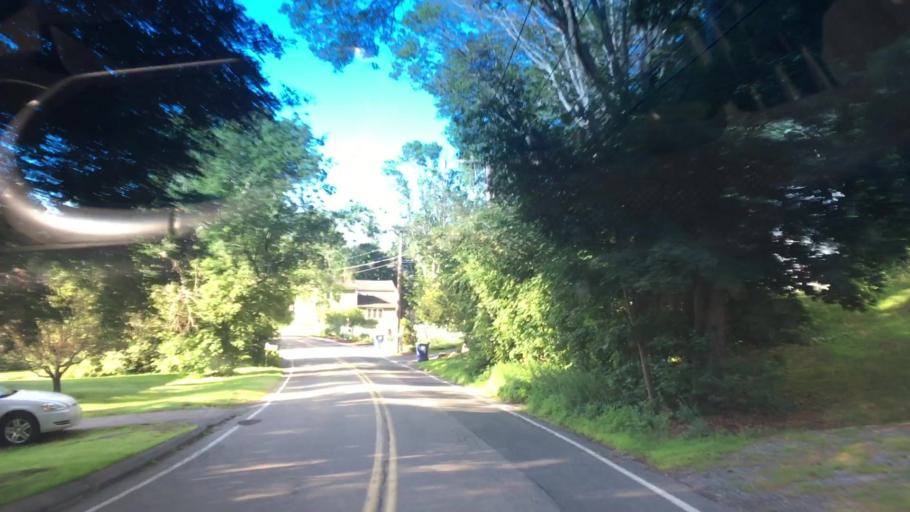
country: US
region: Massachusetts
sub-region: Norfolk County
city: Medway
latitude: 42.1423
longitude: -71.3934
